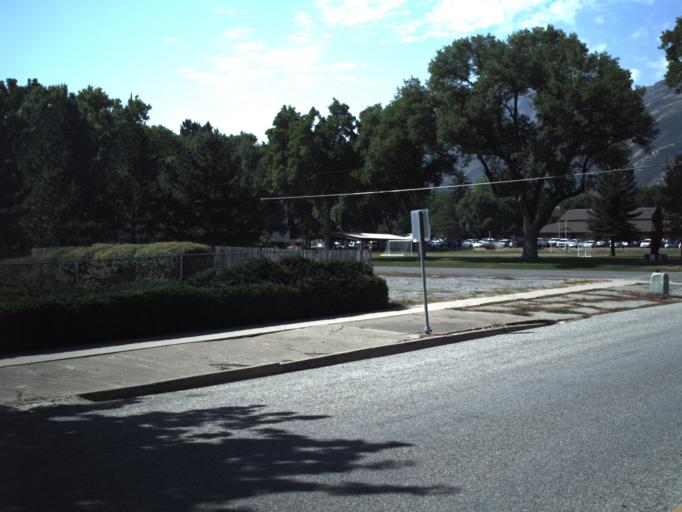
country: US
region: Utah
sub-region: Cache County
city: Wellsville
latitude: 41.6387
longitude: -111.9309
